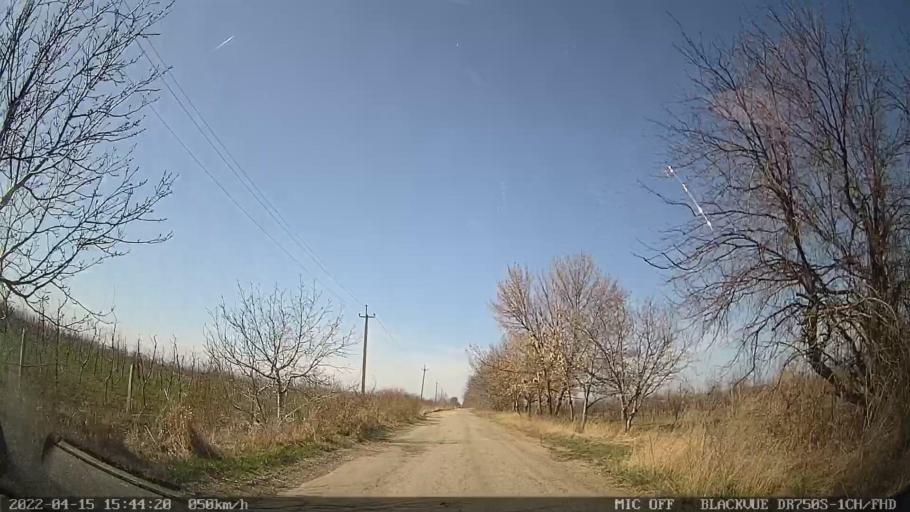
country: MD
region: Raionul Ocnita
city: Otaci
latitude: 48.3698
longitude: 27.9228
